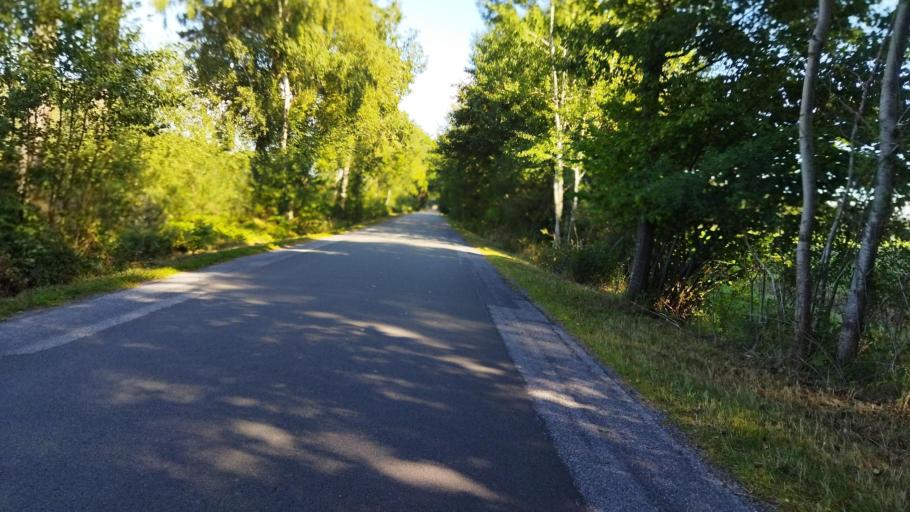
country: DE
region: Lower Saxony
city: Ohne
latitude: 52.2919
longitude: 7.3157
